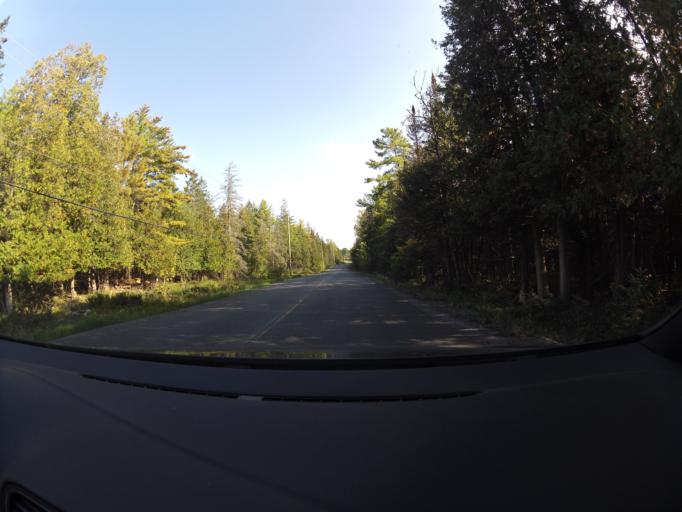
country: CA
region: Ontario
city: Arnprior
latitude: 45.4363
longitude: -76.2466
